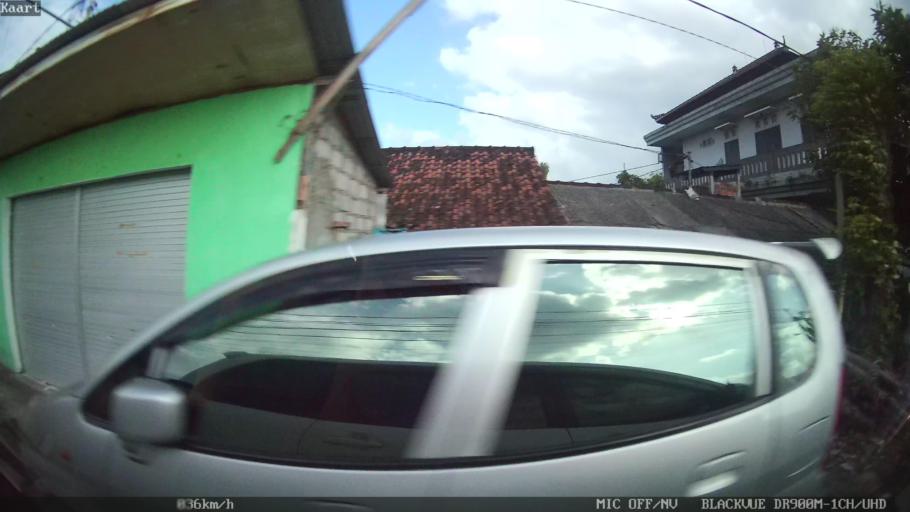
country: ID
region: Bali
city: Karyadharma
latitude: -8.6979
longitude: 115.1948
